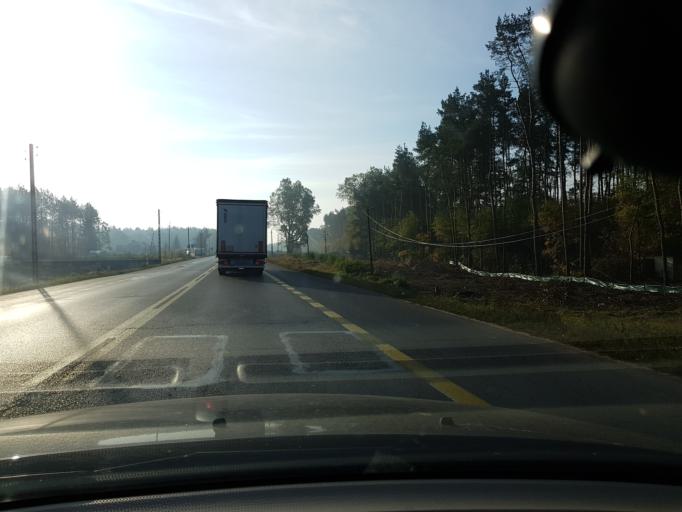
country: PL
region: Masovian Voivodeship
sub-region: Powiat otwocki
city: Otwock
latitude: 52.1453
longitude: 21.3242
